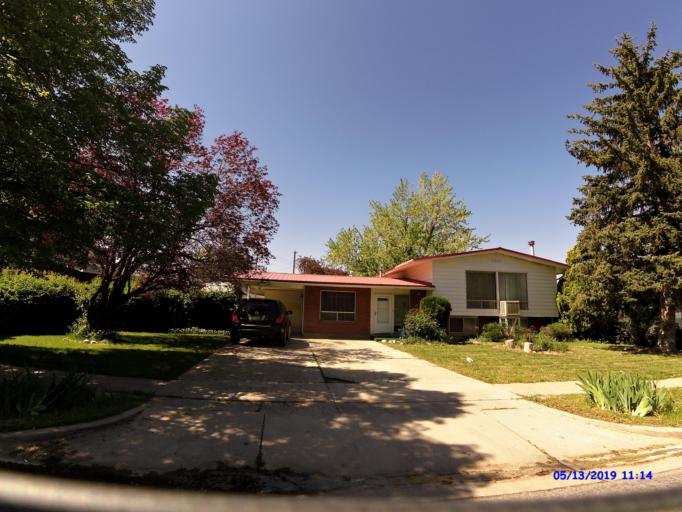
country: US
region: Utah
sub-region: Weber County
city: Harrisville
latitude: 41.2798
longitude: -111.9644
